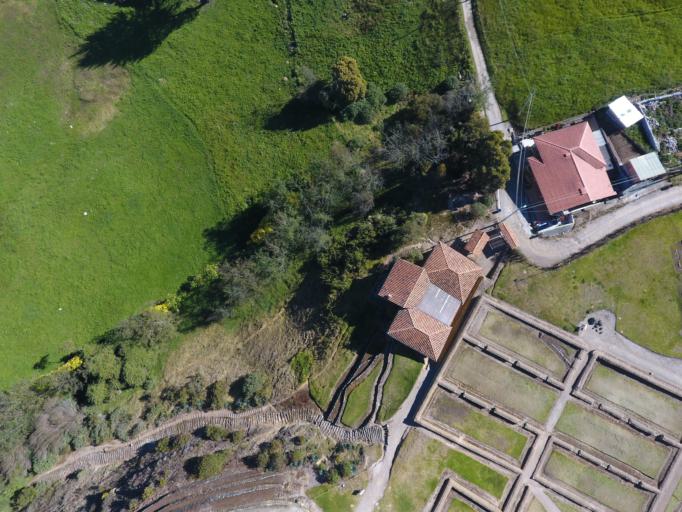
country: EC
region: Canar
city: Canar
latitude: -2.5395
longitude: -78.8745
